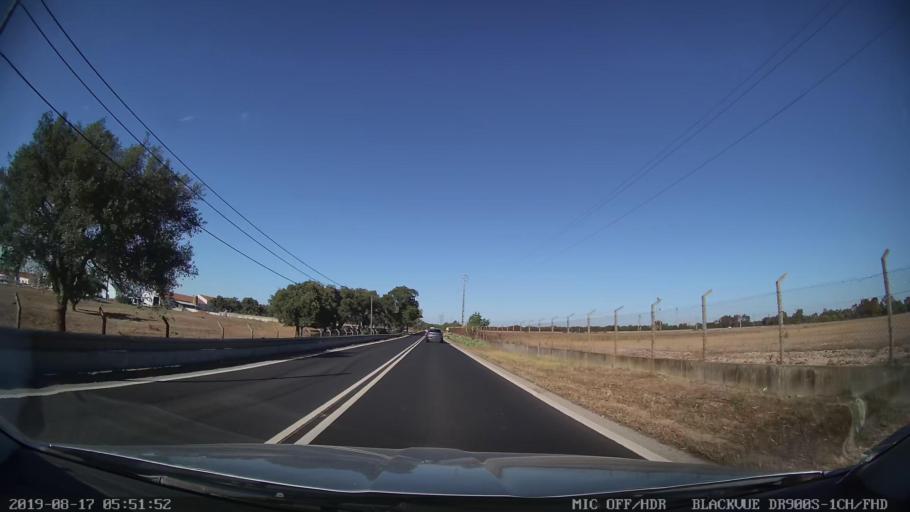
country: PT
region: Setubal
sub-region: Alcochete
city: Alcochete
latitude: 38.7700
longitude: -8.8932
